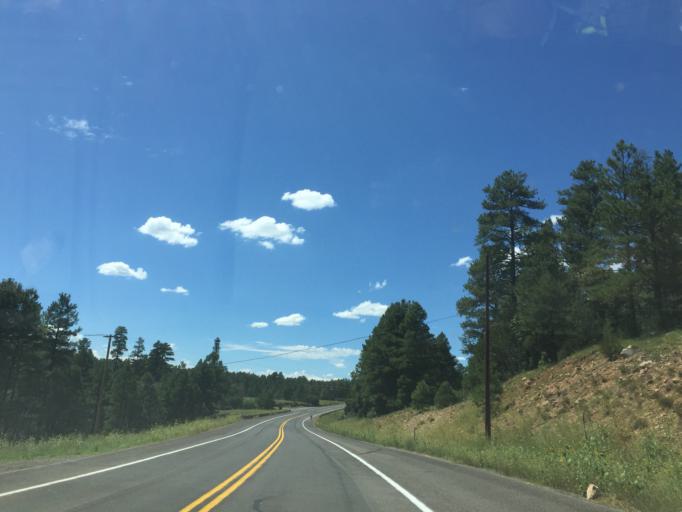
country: US
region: Arizona
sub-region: Coconino County
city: Mountainaire
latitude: 35.1133
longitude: -111.5838
